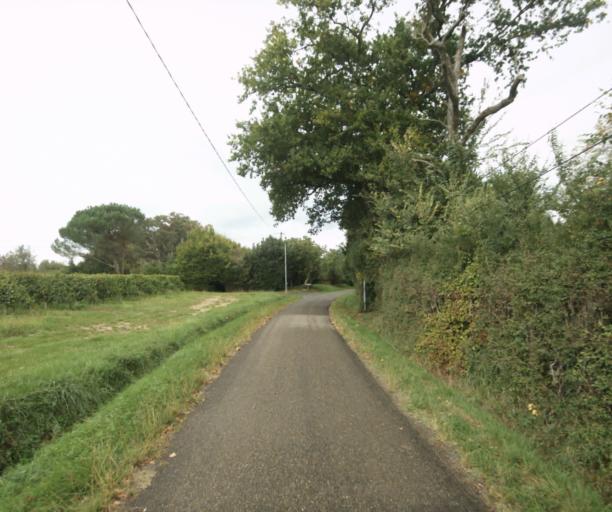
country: FR
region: Midi-Pyrenees
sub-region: Departement du Gers
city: Cazaubon
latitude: 43.8945
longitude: -0.1061
